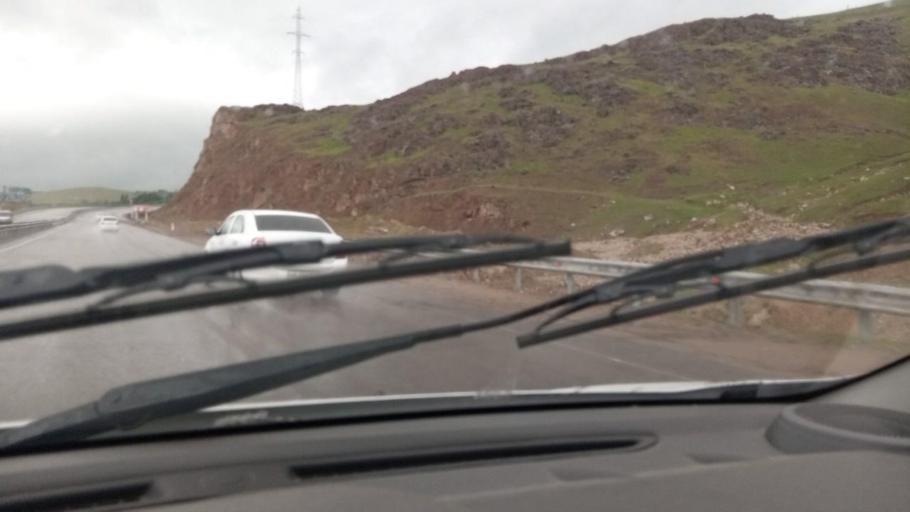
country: UZ
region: Toshkent
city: Angren
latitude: 41.0720
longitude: 70.2740
